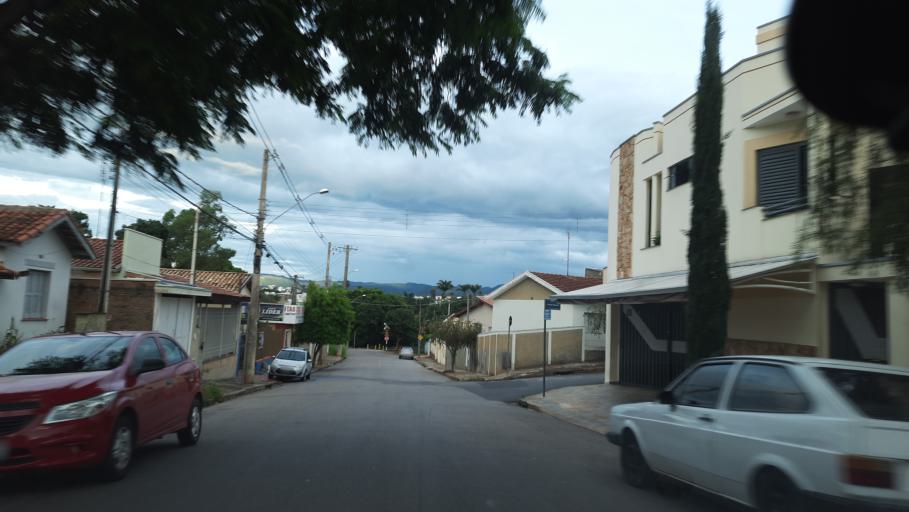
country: BR
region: Sao Paulo
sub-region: Sao Joao Da Boa Vista
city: Sao Joao da Boa Vista
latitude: -21.9640
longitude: -46.7894
